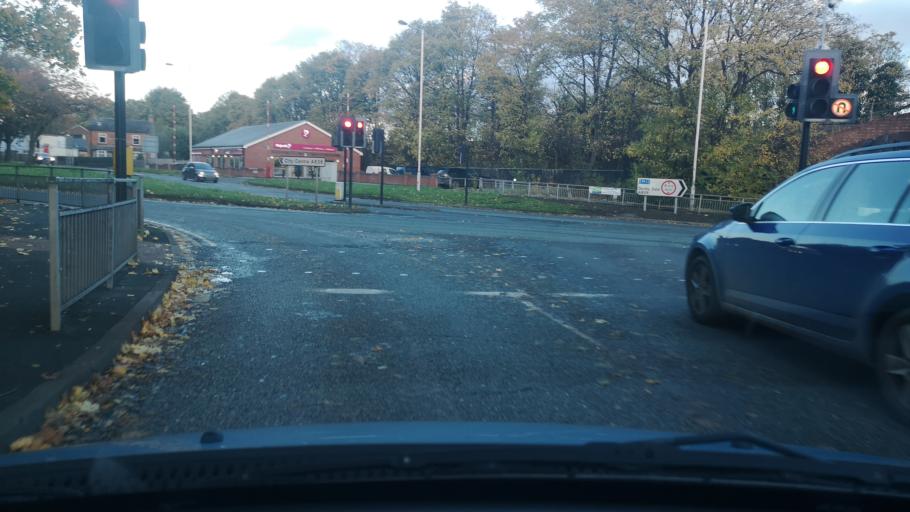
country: GB
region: England
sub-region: City and Borough of Wakefield
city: Wakefield
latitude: 53.6695
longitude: -1.5057
